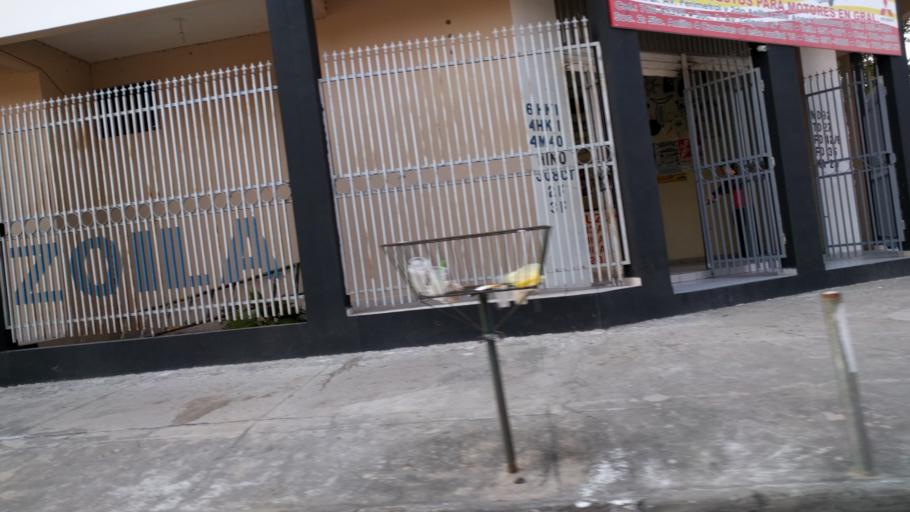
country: BO
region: Santa Cruz
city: Santa Cruz de la Sierra
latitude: -17.8002
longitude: -63.1917
